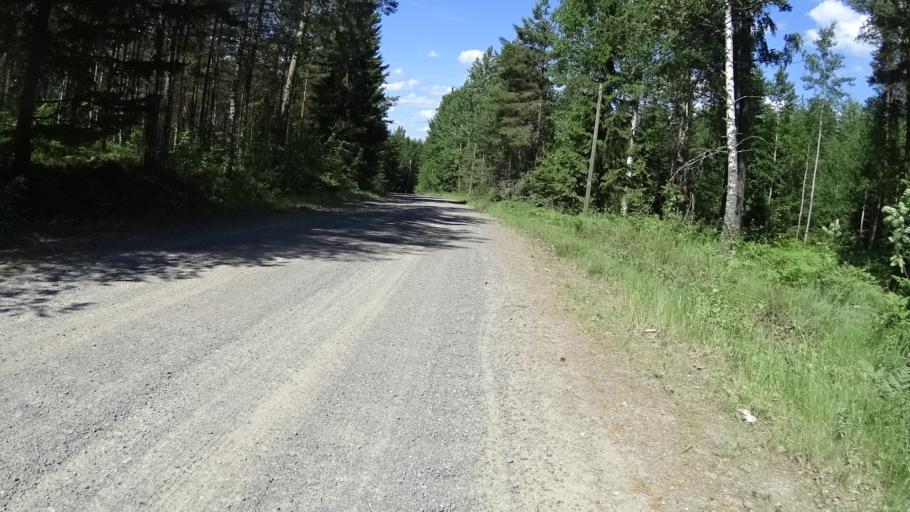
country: FI
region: Uusimaa
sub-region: Raaseporin
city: Pohja
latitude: 60.0974
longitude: 23.5607
